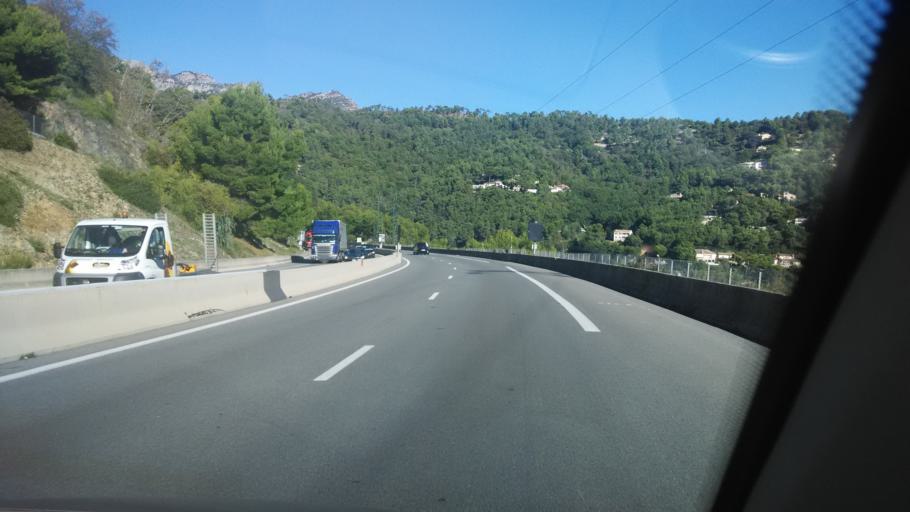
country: MC
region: Commune de Monaco
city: Saint-Roman
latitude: 43.7649
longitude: 7.4497
